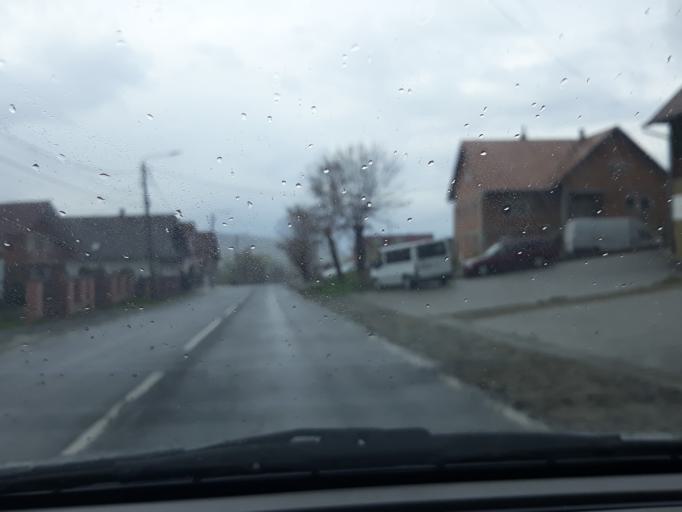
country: RO
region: Harghita
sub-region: Comuna Corund
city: Corund
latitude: 46.4784
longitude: 25.1747
